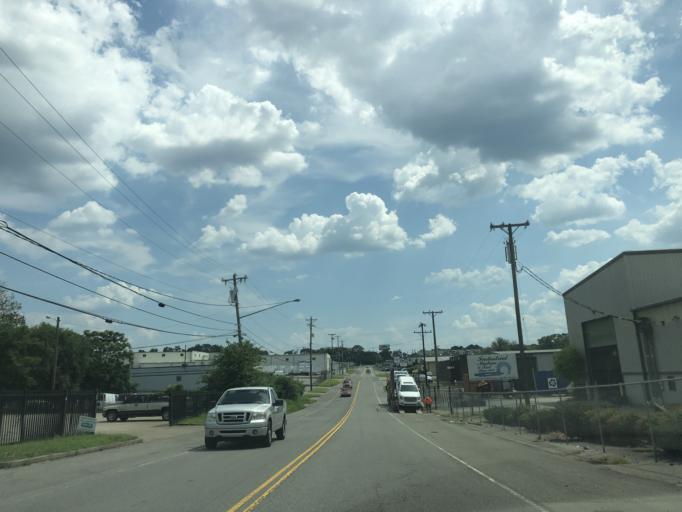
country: US
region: Tennessee
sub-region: Davidson County
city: Nashville
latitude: 36.1409
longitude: -86.7430
